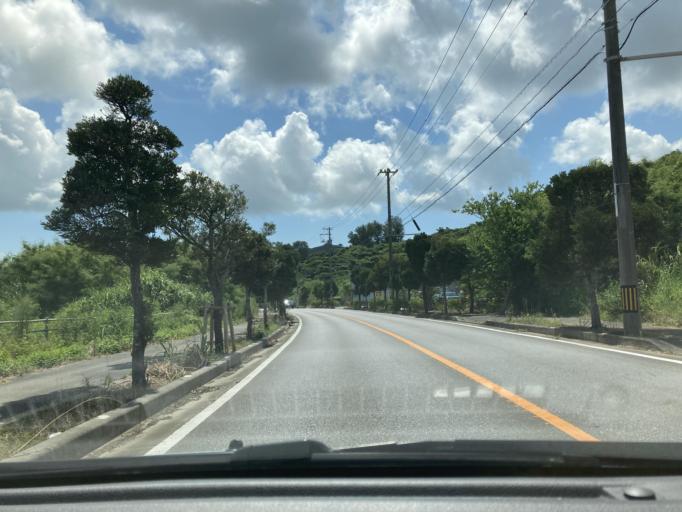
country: JP
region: Okinawa
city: Tomigusuku
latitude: 26.1743
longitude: 127.7682
